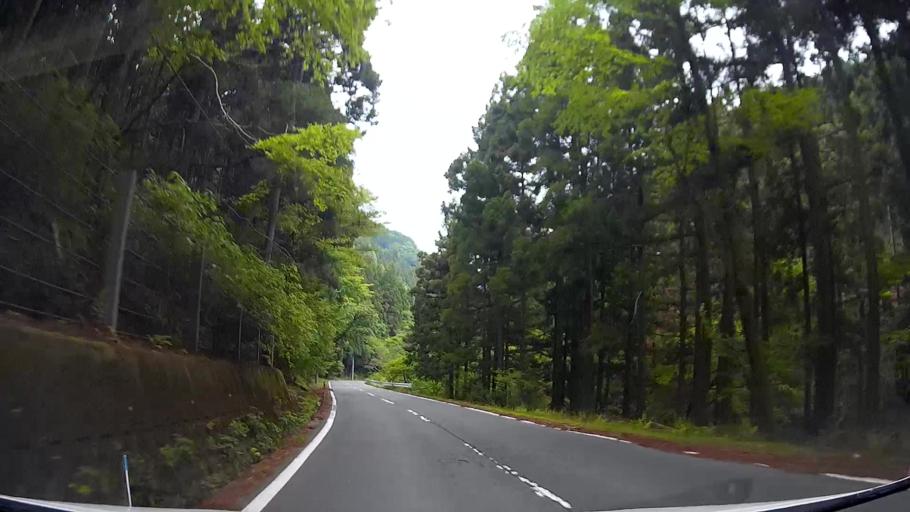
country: JP
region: Shizuoka
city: Ito
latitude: 34.9193
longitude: 139.0438
